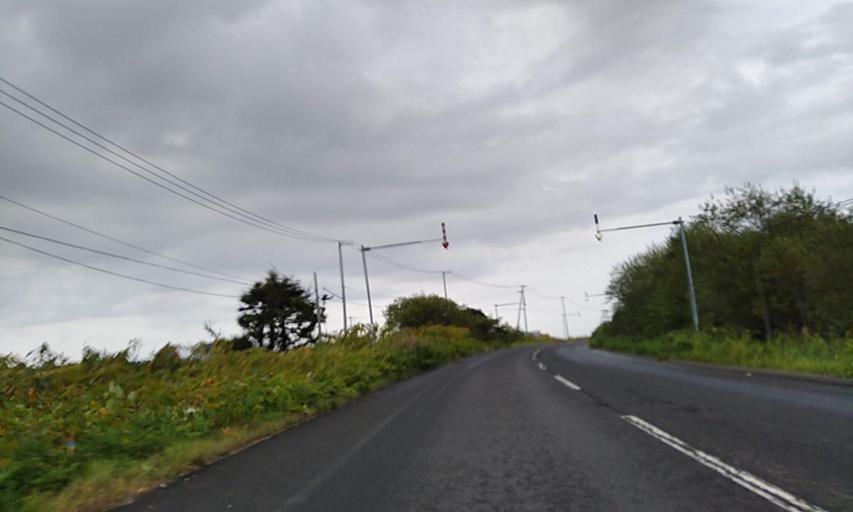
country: JP
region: Hokkaido
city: Mombetsu
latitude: 44.6192
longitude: 142.9229
